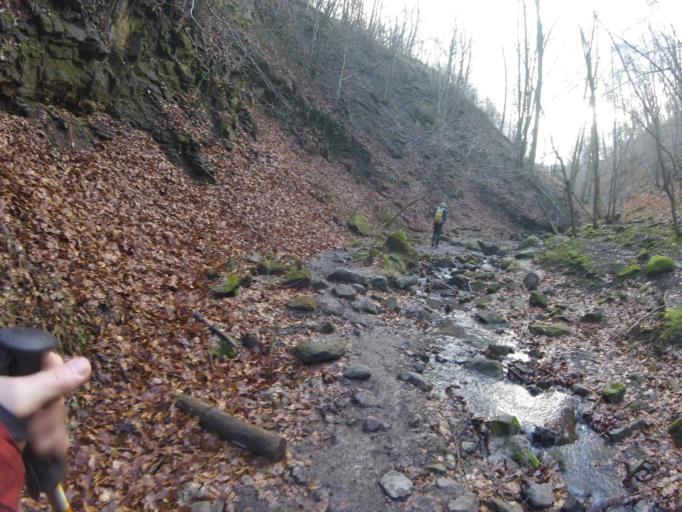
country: HU
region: Komarom-Esztergom
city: Pilismarot
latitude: 47.7407
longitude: 18.8942
